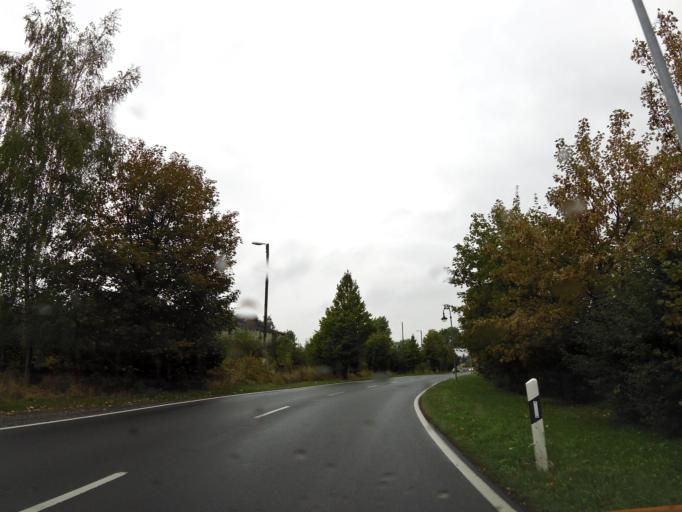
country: DE
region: Saxony-Anhalt
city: Ballenstedt
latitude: 51.7250
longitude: 11.2530
